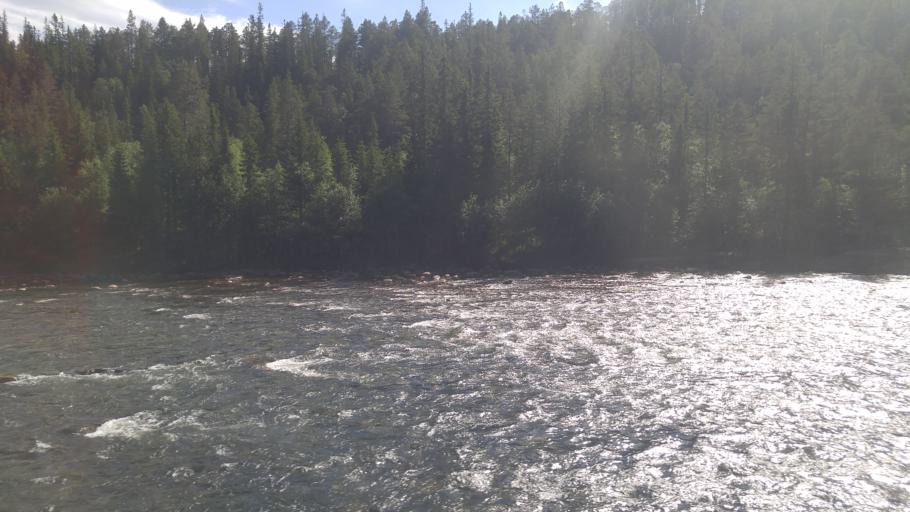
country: NO
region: Sor-Trondelag
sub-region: Selbu
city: Mebonden
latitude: 62.9645
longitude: 10.9684
